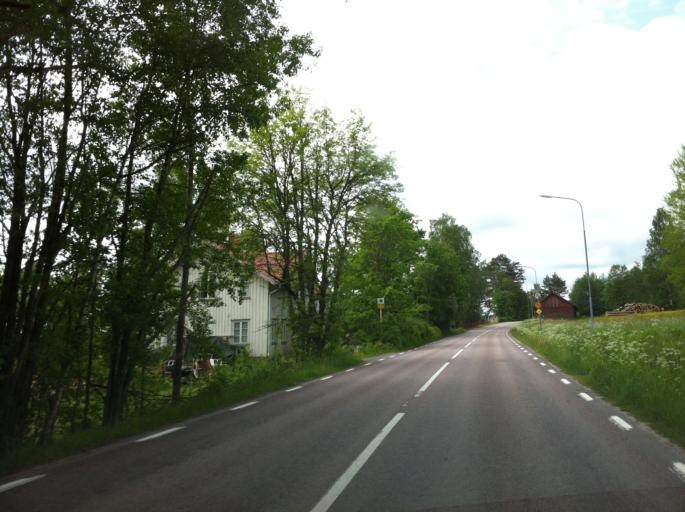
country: SE
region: Vaermland
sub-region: Sunne Kommun
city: Sunne
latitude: 59.8785
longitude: 13.1744
